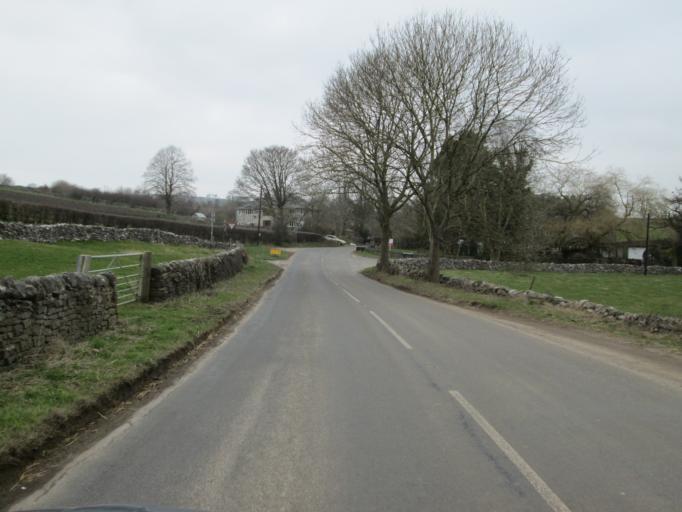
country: GB
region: England
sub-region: Derbyshire
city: Bakewell
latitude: 53.2285
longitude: -1.7108
